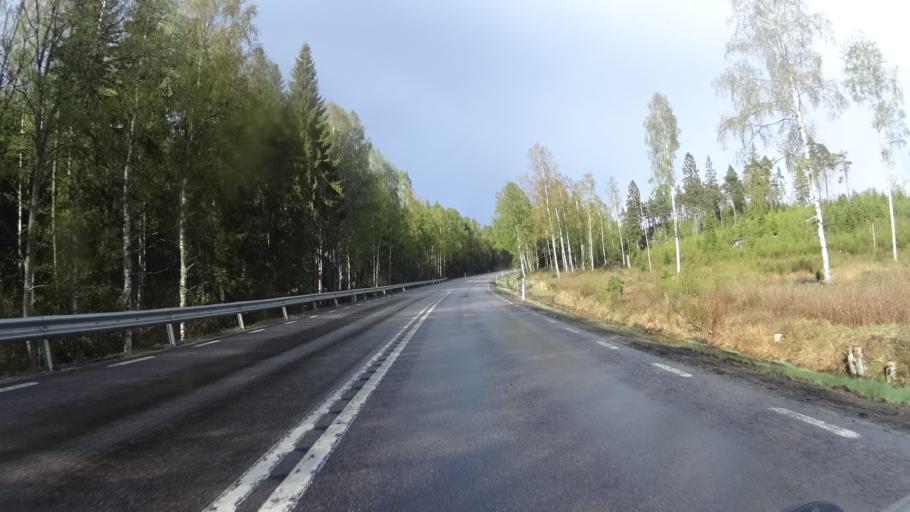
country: SE
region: OErebro
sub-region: Askersunds Kommun
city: Askersund
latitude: 58.7433
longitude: 14.7812
